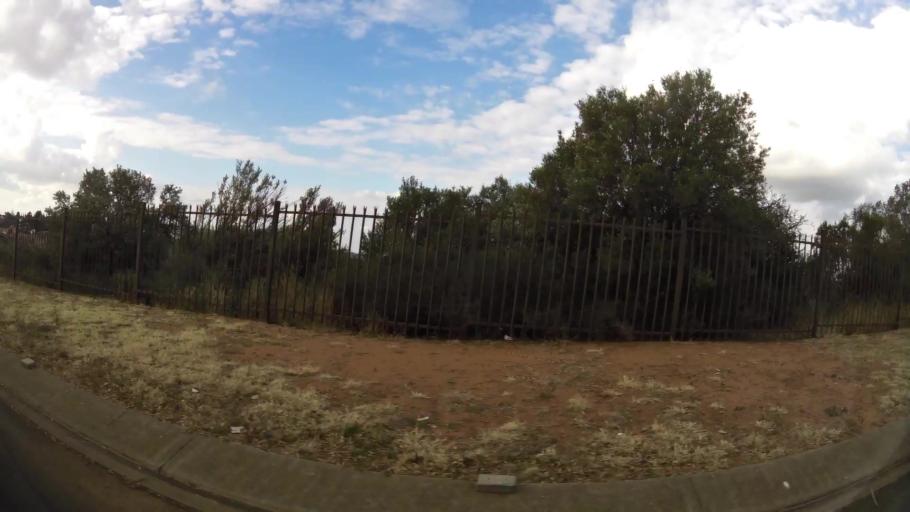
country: ZA
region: Orange Free State
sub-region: Mangaung Metropolitan Municipality
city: Bloemfontein
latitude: -29.0885
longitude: 26.2021
